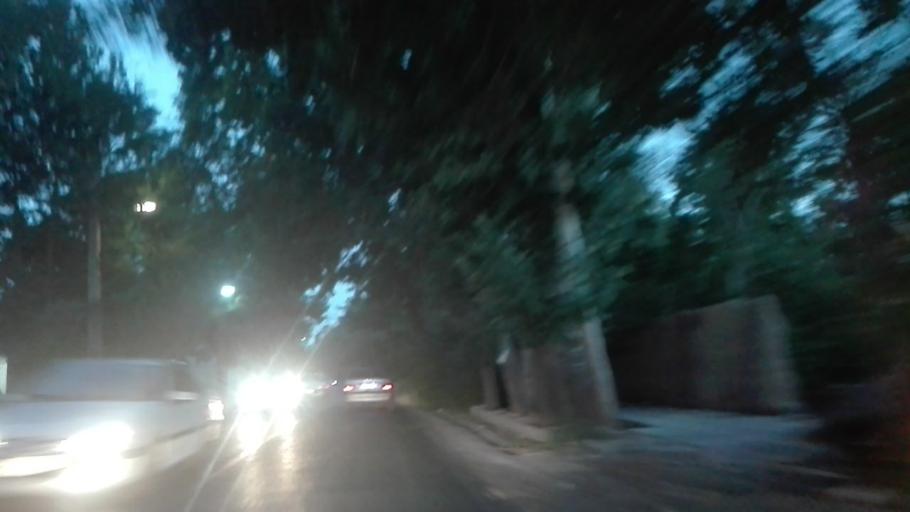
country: IR
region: Tehran
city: Shahriar
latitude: 35.6438
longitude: 51.0557
